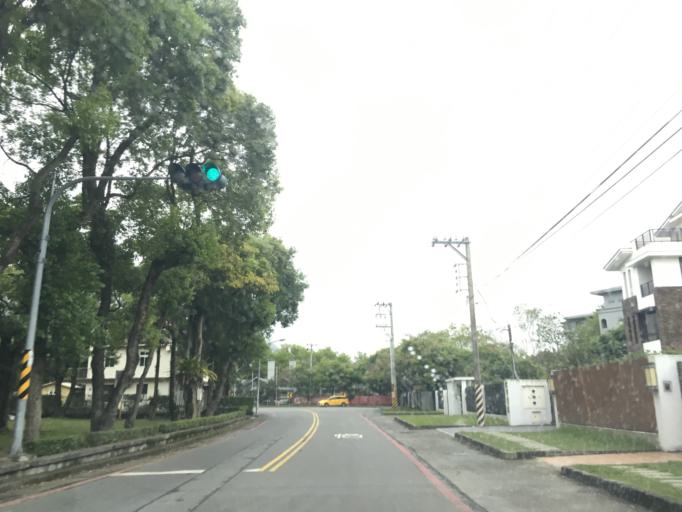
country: TW
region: Taiwan
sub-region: Hualien
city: Hualian
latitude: 23.9965
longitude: 121.5742
